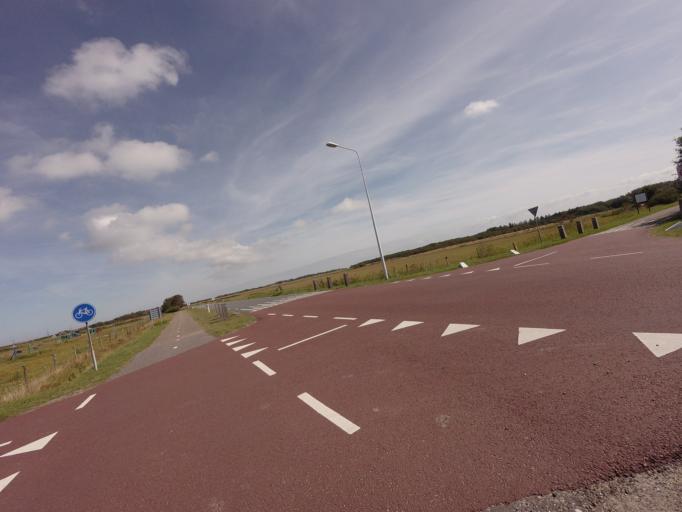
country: NL
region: Friesland
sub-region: Gemeente Ameland
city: Hollum
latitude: 53.4459
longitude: 5.6616
